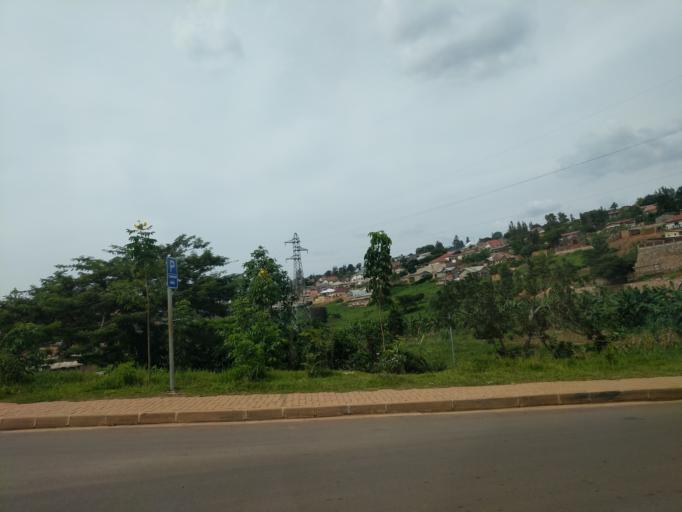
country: RW
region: Kigali
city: Kigali
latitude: -1.9745
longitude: 30.1190
